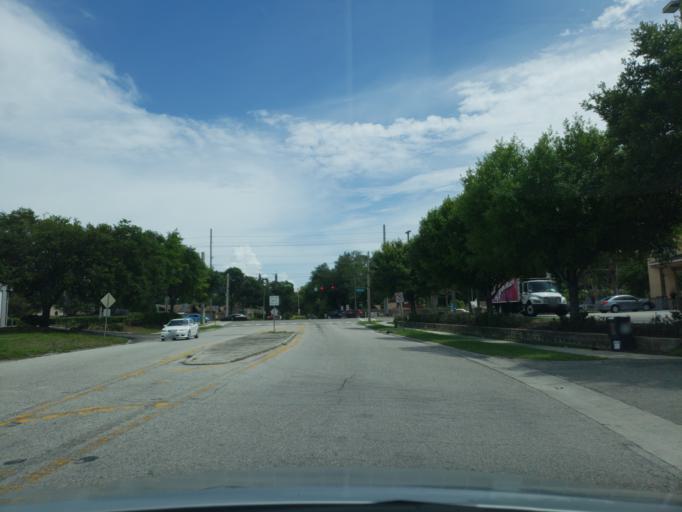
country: US
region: Florida
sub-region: Hillsborough County
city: Town 'n' Country
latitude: 28.0266
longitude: -82.5516
